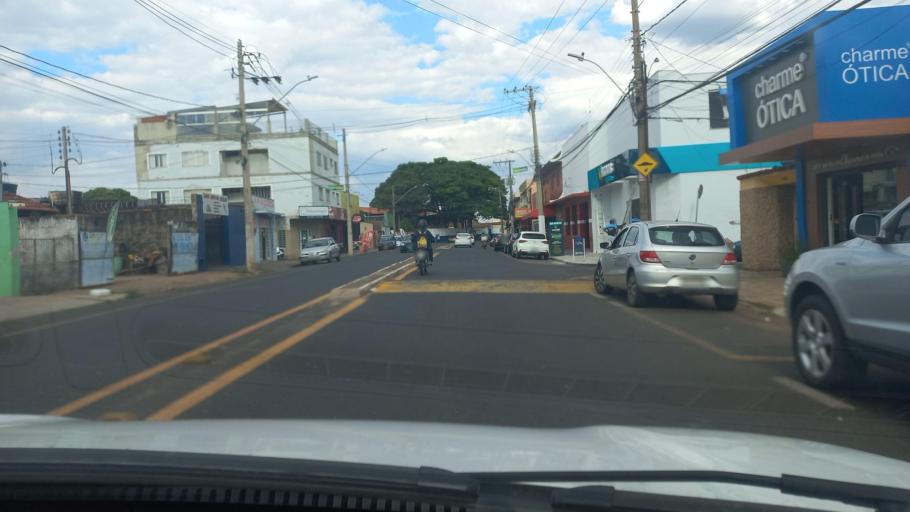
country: BR
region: Minas Gerais
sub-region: Uberaba
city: Uberaba
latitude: -19.7344
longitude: -47.9213
